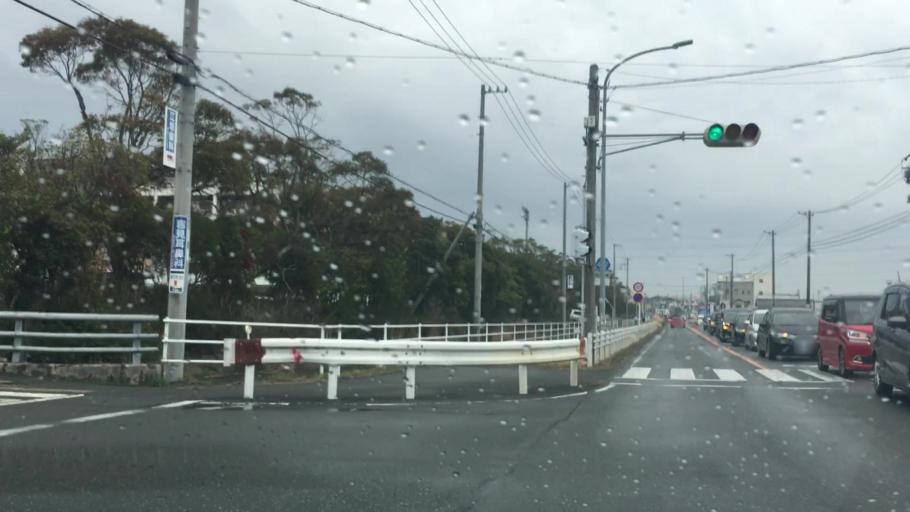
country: JP
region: Aichi
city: Toyohashi
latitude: 34.7103
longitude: 137.3865
